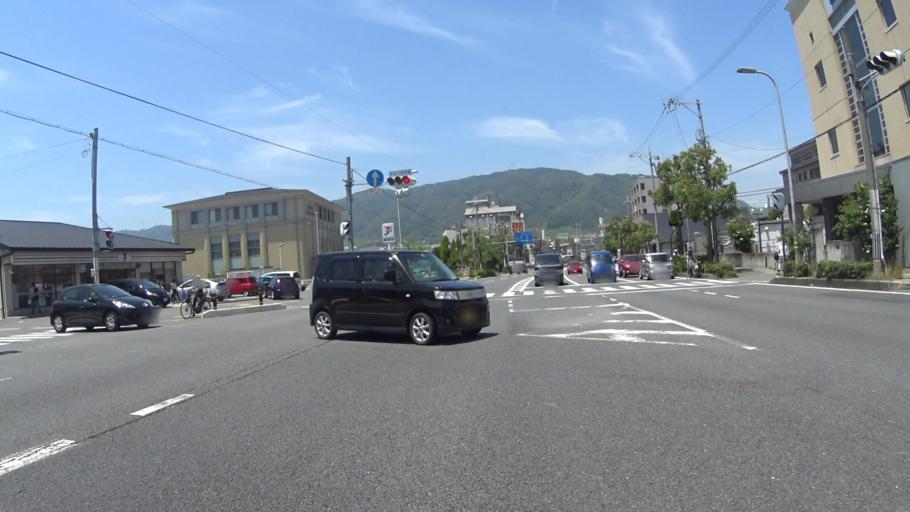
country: JP
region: Kyoto
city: Kameoka
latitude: 35.0614
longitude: 135.5454
